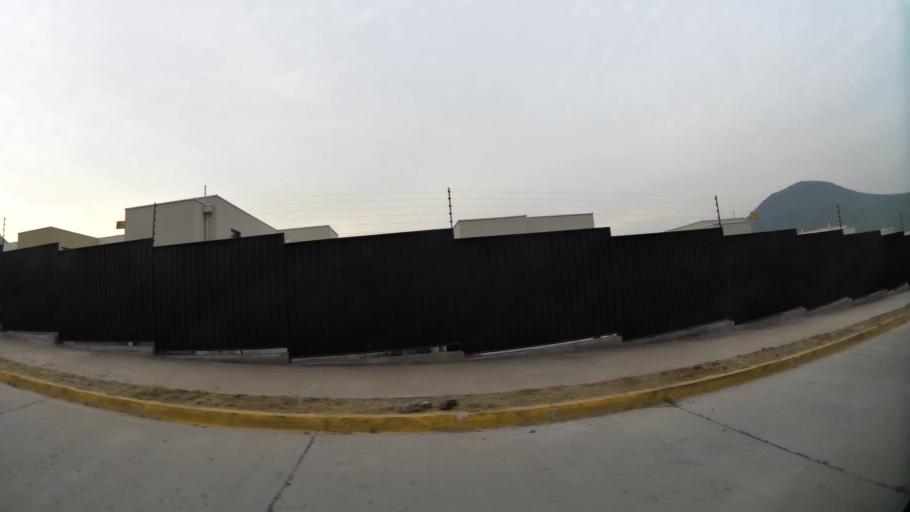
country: CL
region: Santiago Metropolitan
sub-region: Provincia de Chacabuco
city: Chicureo Abajo
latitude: -33.3231
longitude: -70.6489
